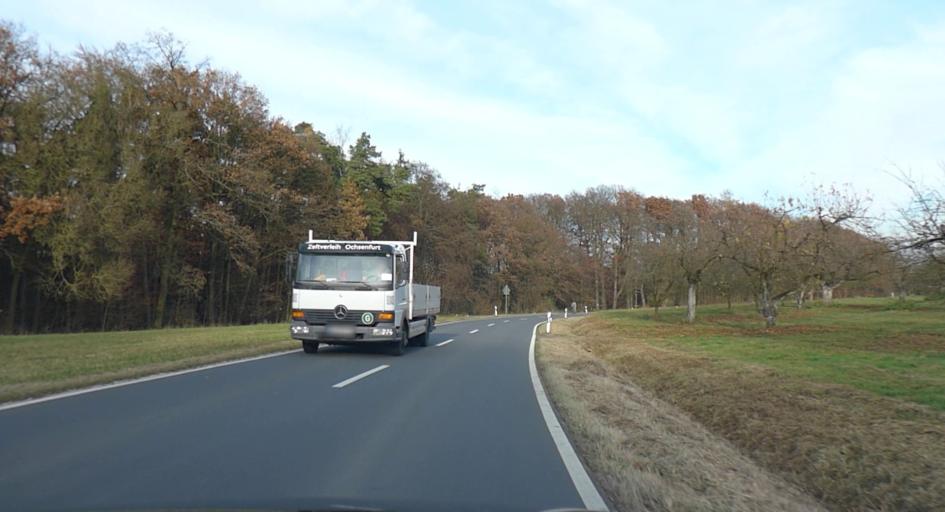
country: DE
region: Bavaria
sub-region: Regierungsbezirk Mittelfranken
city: Bubenreuth
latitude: 49.6211
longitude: 11.0314
